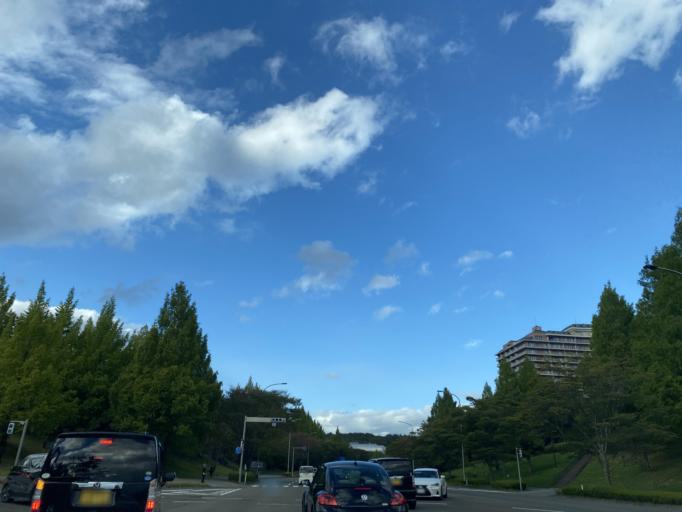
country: JP
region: Miyagi
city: Tomiya
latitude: 38.3401
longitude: 140.8387
